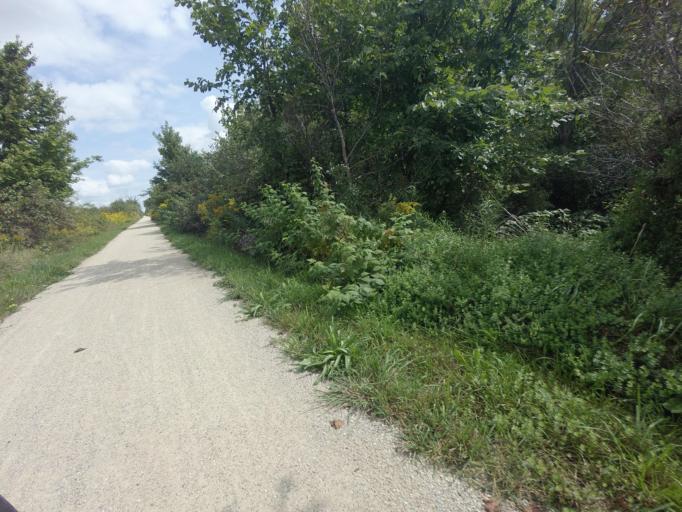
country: CA
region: Ontario
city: North Perth
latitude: 43.5752
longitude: -80.8220
